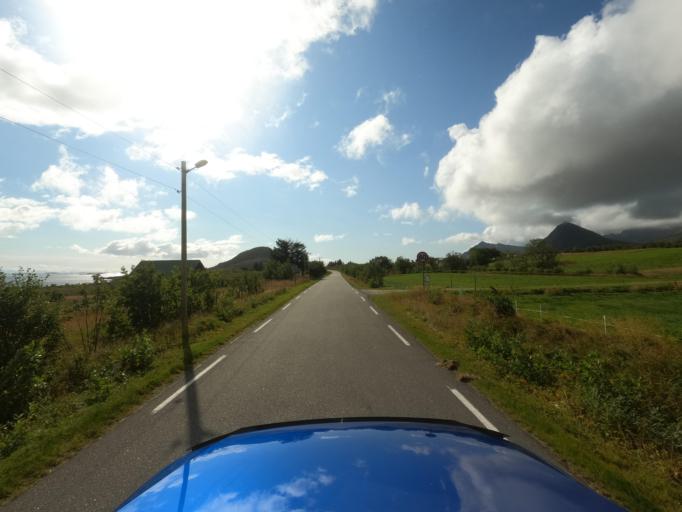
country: NO
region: Nordland
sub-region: Vagan
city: Kabelvag
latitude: 68.2388
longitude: 14.1167
